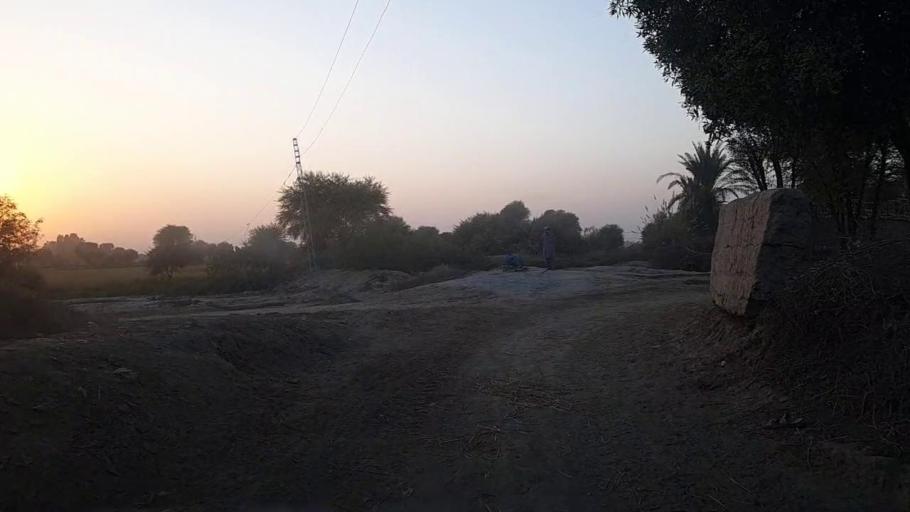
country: PK
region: Sindh
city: Kashmor
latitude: 28.4195
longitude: 69.4484
